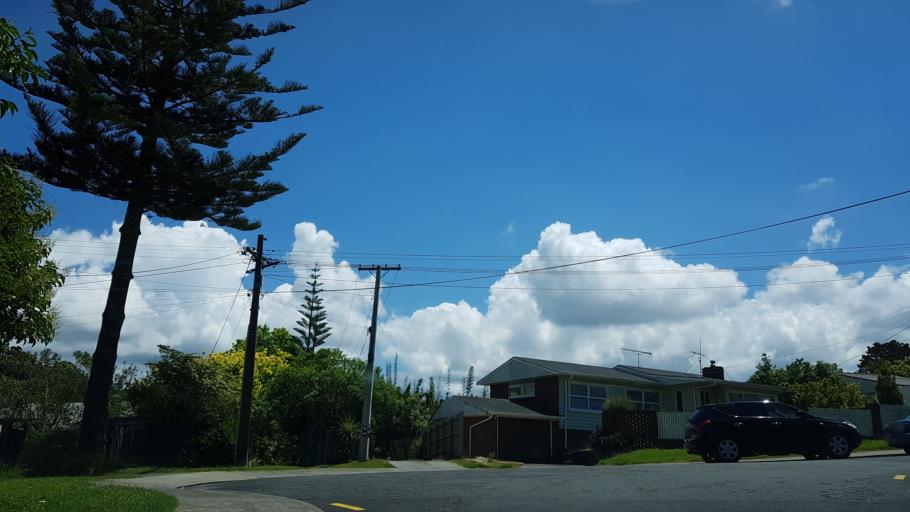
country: NZ
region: Auckland
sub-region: Auckland
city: North Shore
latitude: -36.7988
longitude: 174.6957
